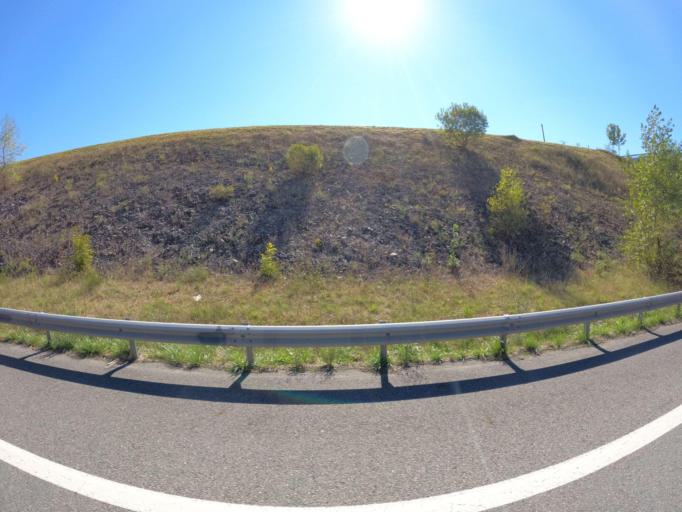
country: FR
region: Limousin
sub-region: Departement de la Creuse
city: Gouzon
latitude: 46.1951
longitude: 2.1605
